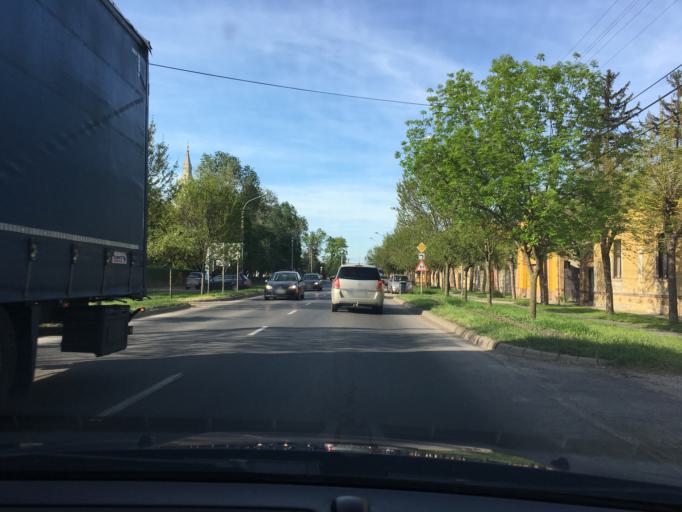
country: HU
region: Bekes
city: Mezobereny
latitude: 46.8270
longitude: 21.0293
